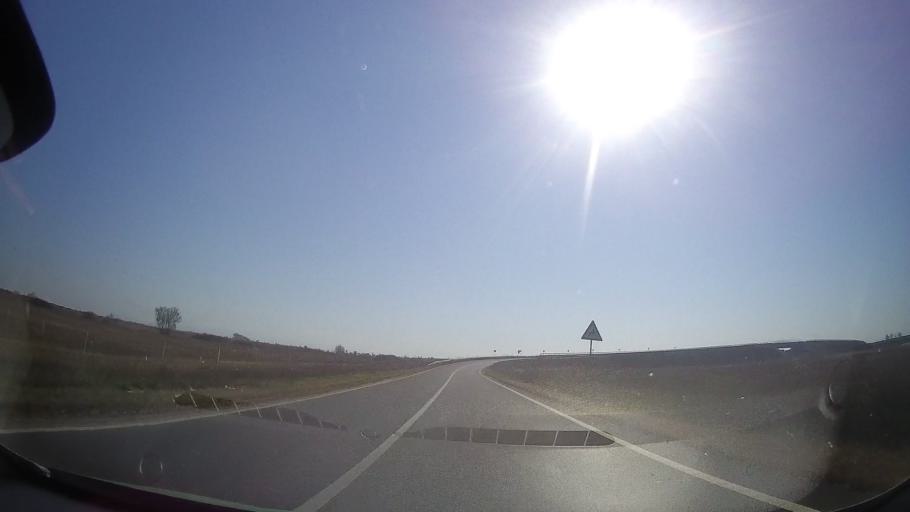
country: RO
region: Timis
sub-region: Comuna Belint
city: Belint
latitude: 45.7837
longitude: 21.7320
